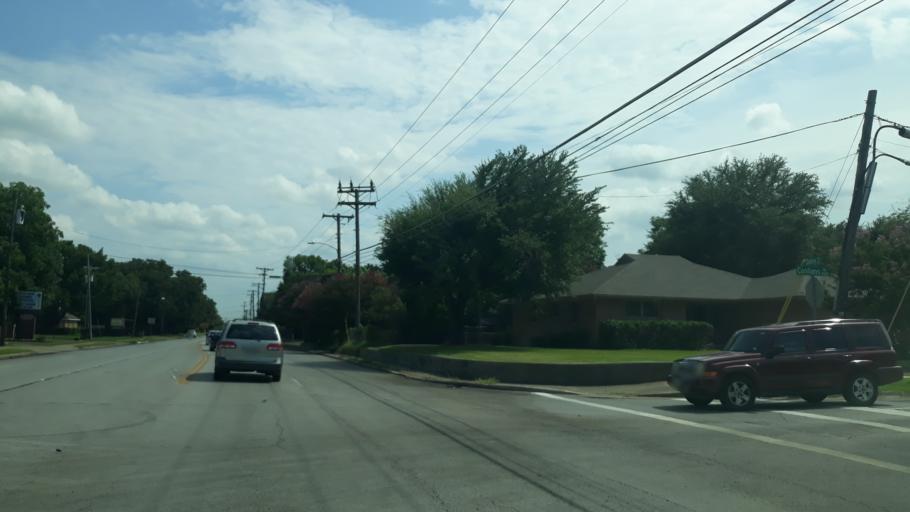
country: US
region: Texas
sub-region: Dallas County
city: Irving
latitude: 32.8218
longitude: -96.9765
